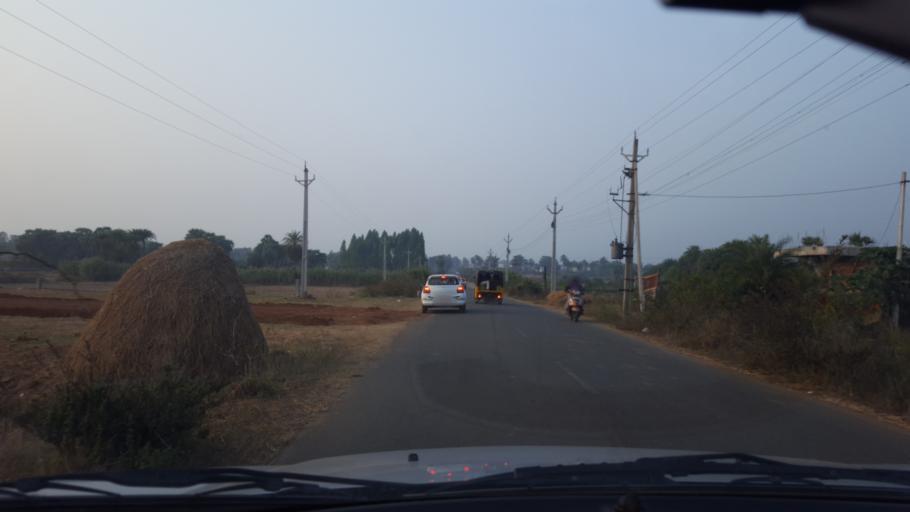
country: IN
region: Andhra Pradesh
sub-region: Srikakulam
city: Amudalavalasa
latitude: 18.3861
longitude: 83.9234
